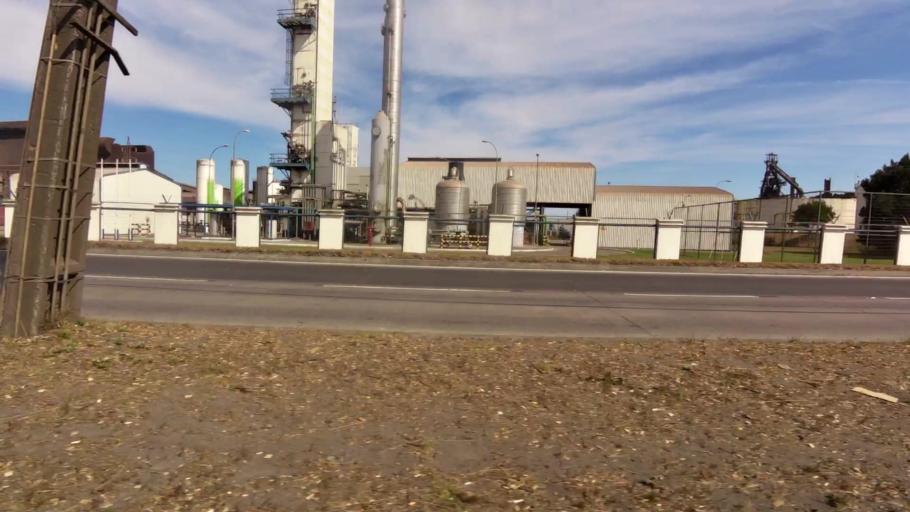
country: CL
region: Biobio
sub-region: Provincia de Concepcion
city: Talcahuano
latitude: -36.7466
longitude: -73.1228
